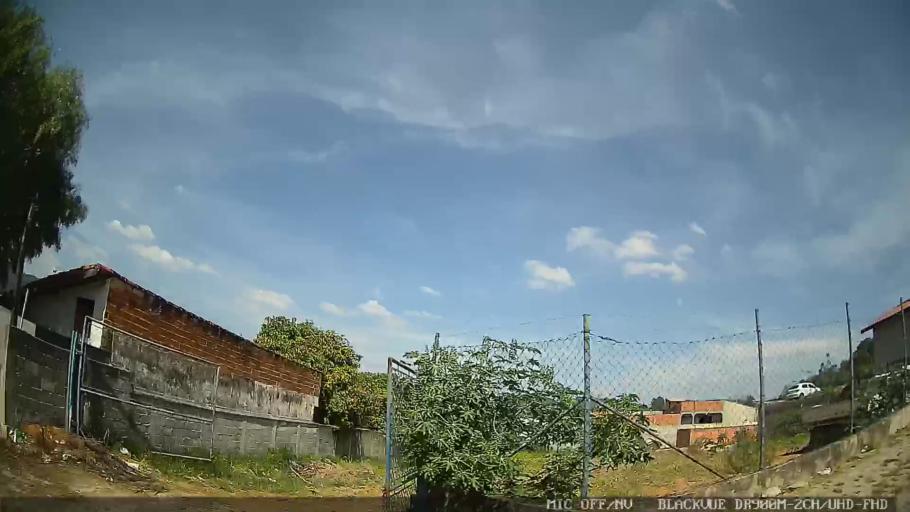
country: BR
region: Sao Paulo
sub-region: Cabreuva
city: Cabreuva
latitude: -23.2722
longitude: -47.0522
